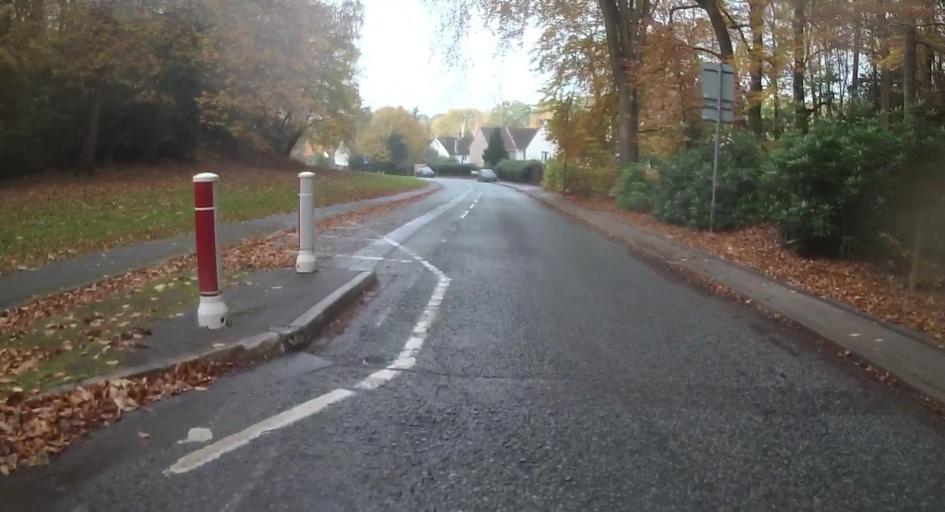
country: GB
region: England
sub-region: Bracknell Forest
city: Crowthorne
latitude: 51.3699
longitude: -0.7837
